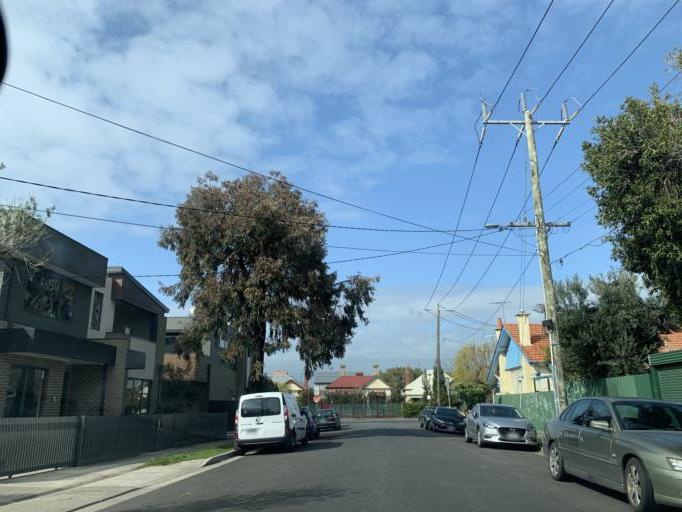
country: AU
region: Victoria
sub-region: Moreland
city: Coburg
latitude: -37.7402
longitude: 144.9609
